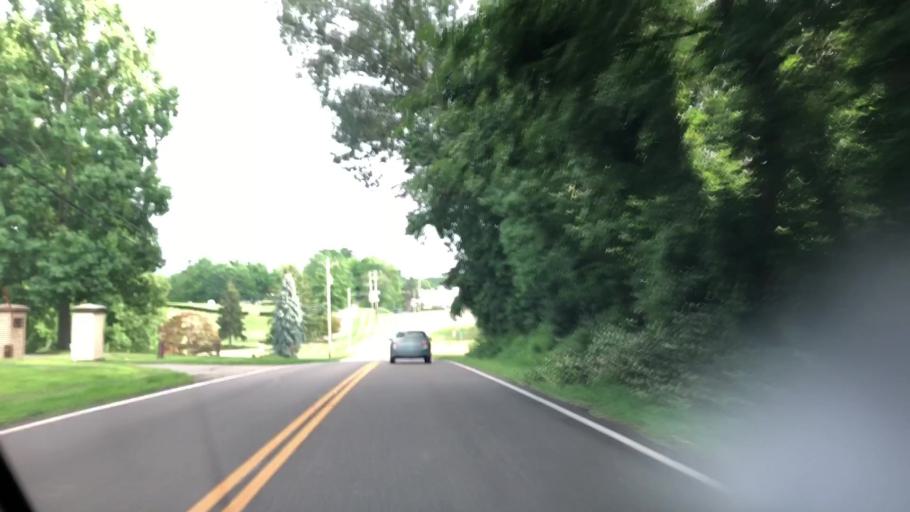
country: US
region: Ohio
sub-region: Stark County
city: North Canton
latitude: 40.8549
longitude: -81.4425
